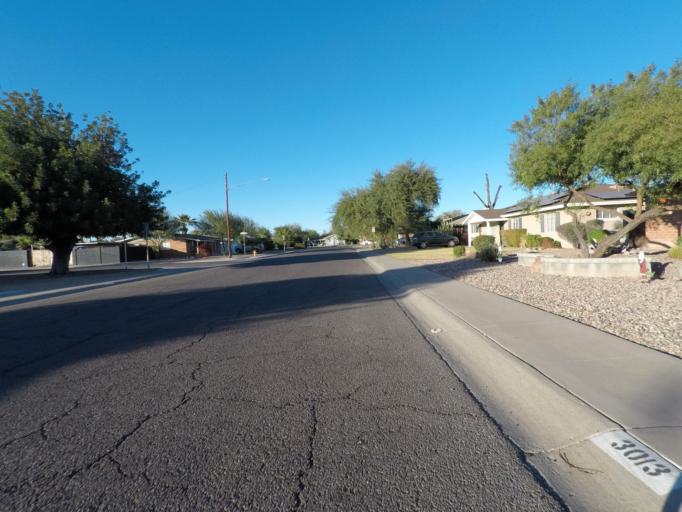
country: US
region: Arizona
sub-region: Maricopa County
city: Phoenix
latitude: 33.4829
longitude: -112.1047
